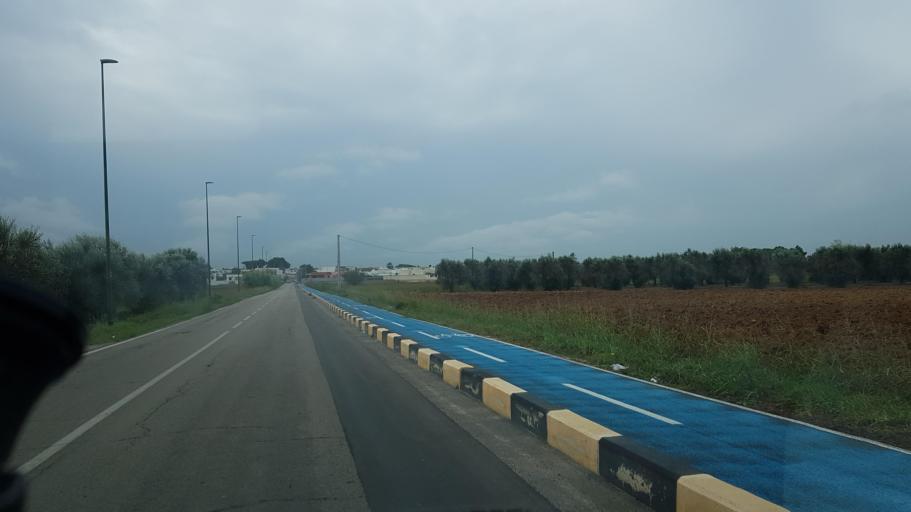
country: IT
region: Apulia
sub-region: Provincia di Lecce
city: Guagnano
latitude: 40.4084
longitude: 17.9554
